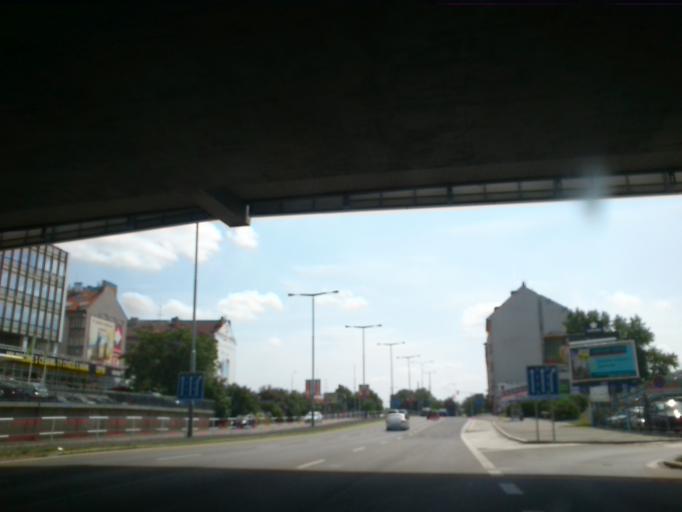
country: CZ
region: Praha
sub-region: Praha 8
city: Karlin
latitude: 50.1098
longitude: 14.4443
